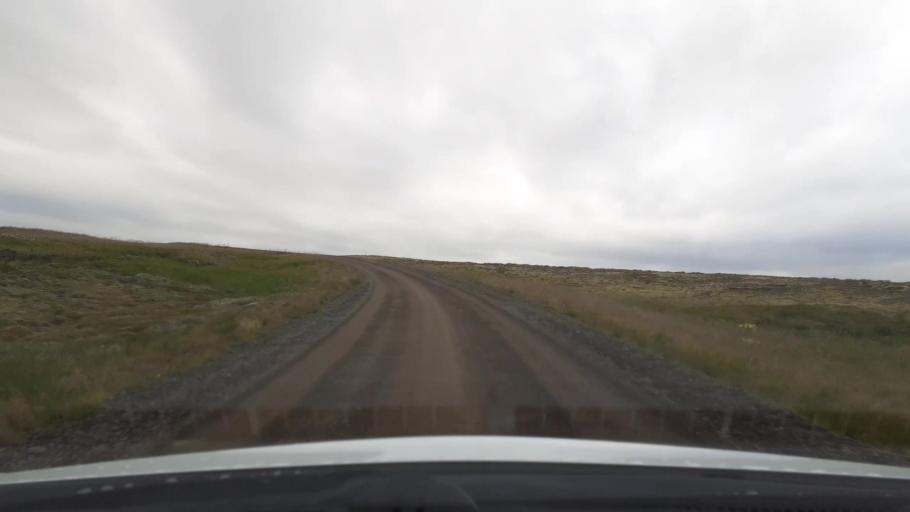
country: IS
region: Capital Region
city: Mosfellsbaer
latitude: 64.1978
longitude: -21.5560
